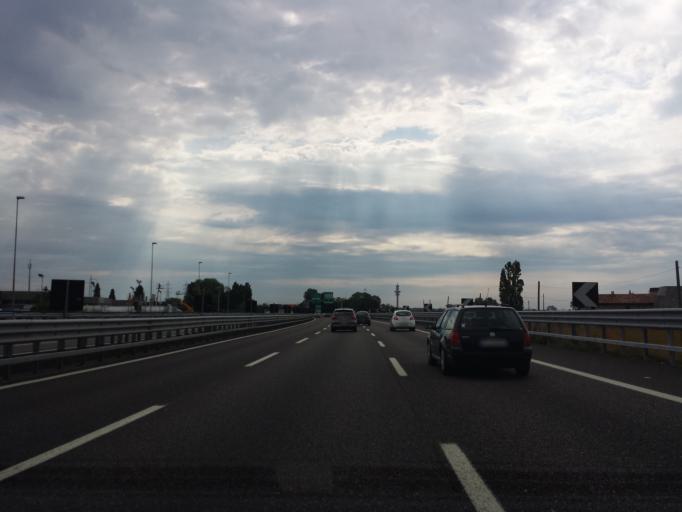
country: IT
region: Lombardy
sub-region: Citta metropolitana di Milano
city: Assago
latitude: 45.3997
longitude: 9.1262
